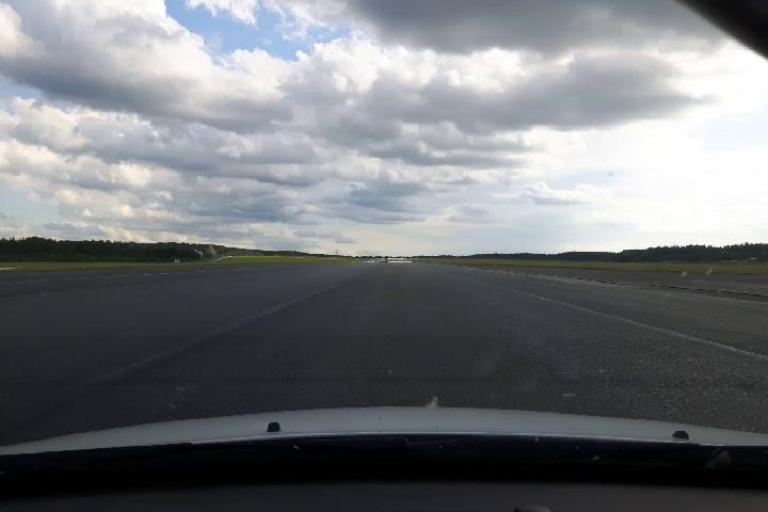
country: SE
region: Stockholm
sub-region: Sigtuna Kommun
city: Rosersberg
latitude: 59.6406
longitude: 17.9557
